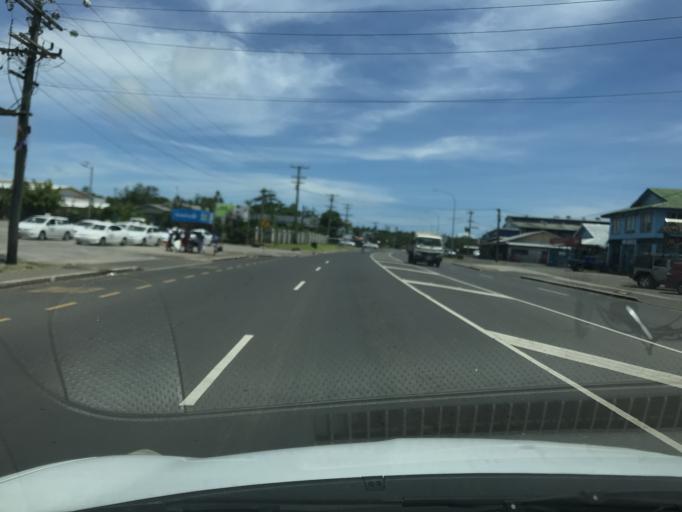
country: WS
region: Tuamasaga
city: Vaiusu
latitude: -13.8196
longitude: -171.8053
